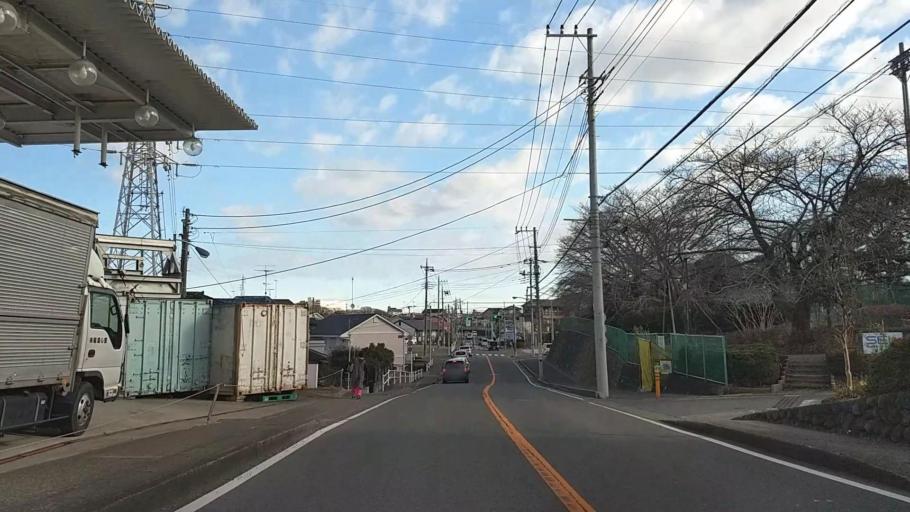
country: JP
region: Kanagawa
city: Atsugi
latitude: 35.4370
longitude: 139.3396
